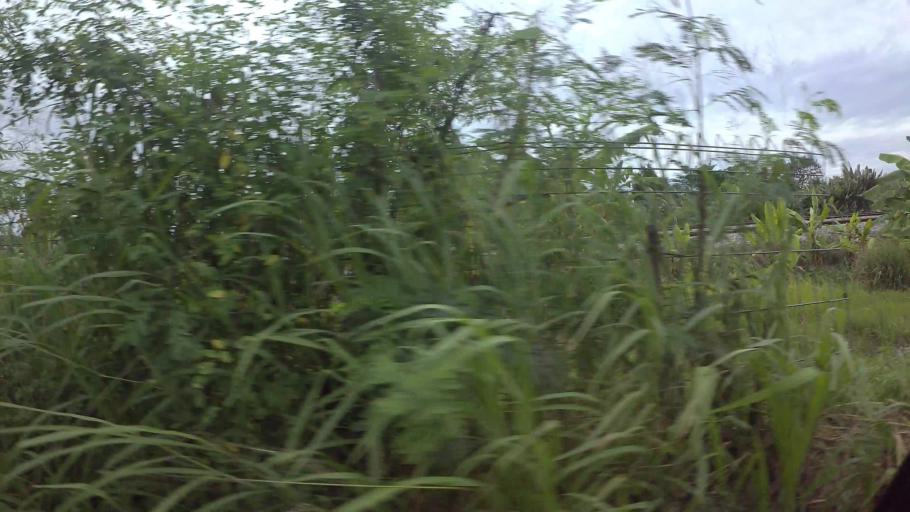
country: TH
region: Chon Buri
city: Si Racha
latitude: 13.1373
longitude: 100.9449
